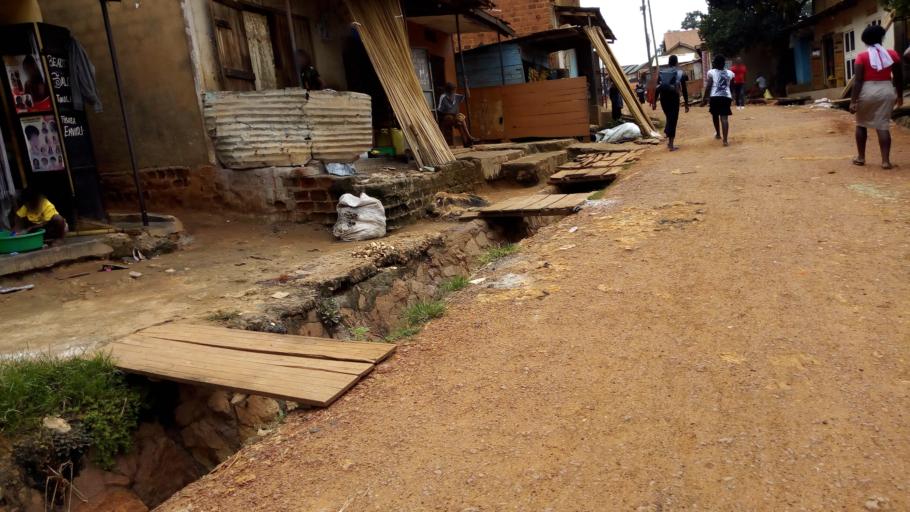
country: UG
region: Central Region
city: Kampala Central Division
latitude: 0.3797
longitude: 32.5595
